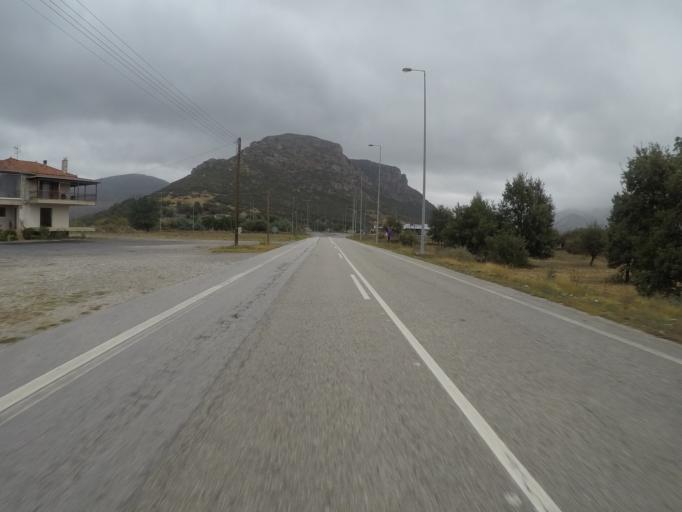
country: GR
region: Peloponnese
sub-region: Nomos Arkadias
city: Tripoli
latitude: 37.5915
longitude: 22.4283
